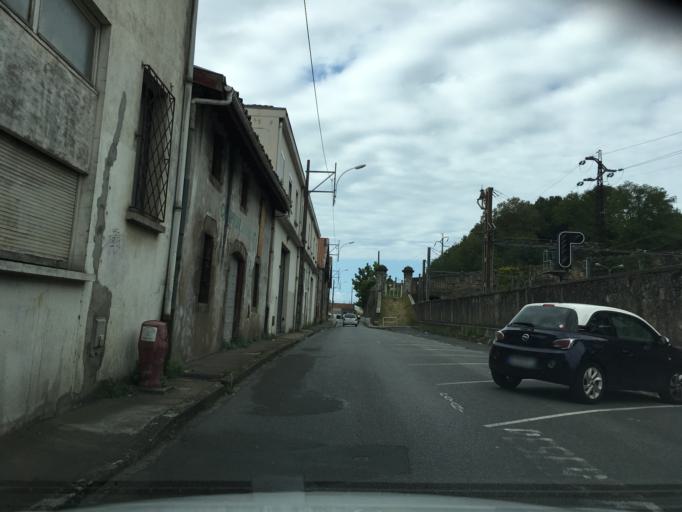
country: FR
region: Aquitaine
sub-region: Departement des Pyrenees-Atlantiques
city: Bayonne
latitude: 43.4965
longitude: -1.4728
